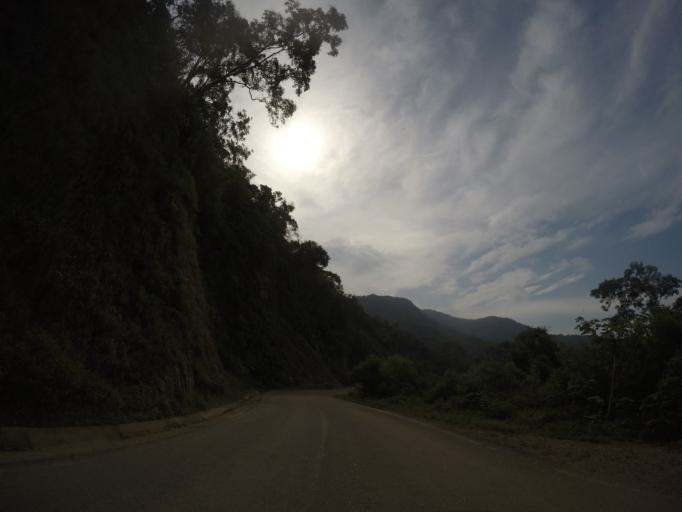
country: MX
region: Oaxaca
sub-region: San Pedro Pochutla
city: Los Naranjos Esquipulas
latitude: 15.9584
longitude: -96.4551
